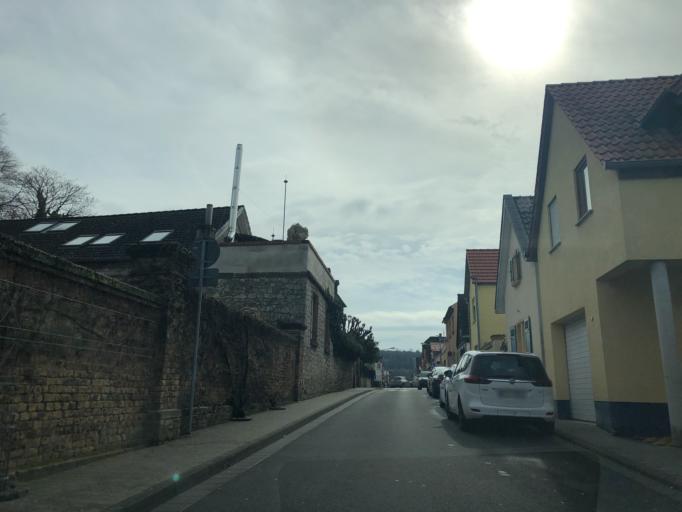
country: DE
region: Rheinland-Pfalz
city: Nierstein
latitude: 49.8705
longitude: 8.3363
